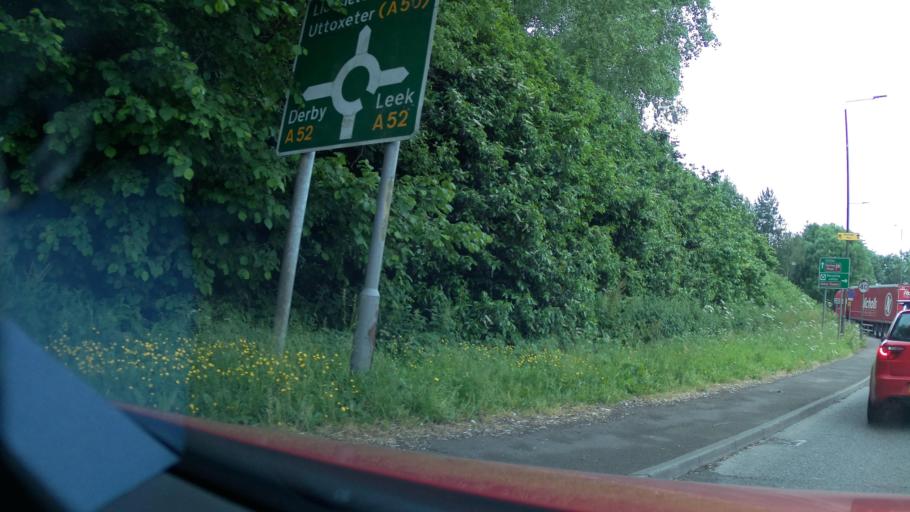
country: GB
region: England
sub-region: Derbyshire
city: Ashbourne
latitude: 53.0093
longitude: -1.7429
